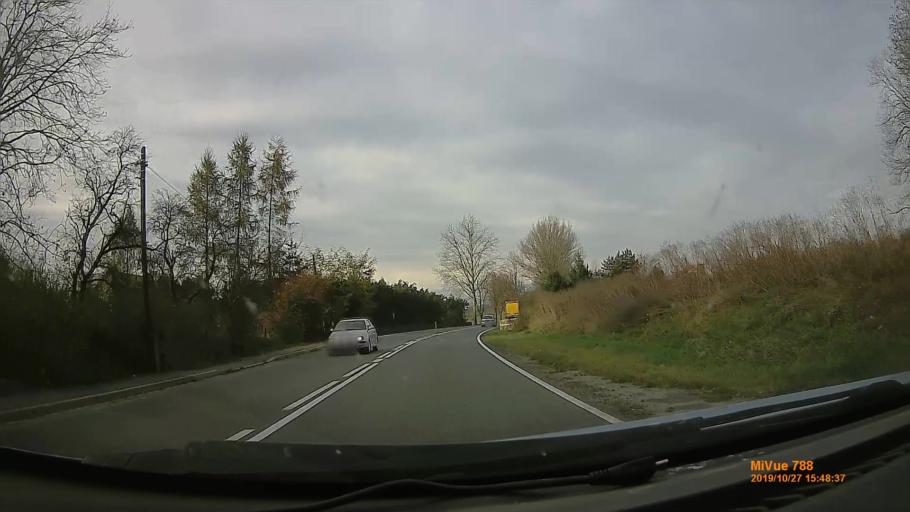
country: PL
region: Lower Silesian Voivodeship
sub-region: Powiat klodzki
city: Bozkow
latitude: 50.4987
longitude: 16.5854
